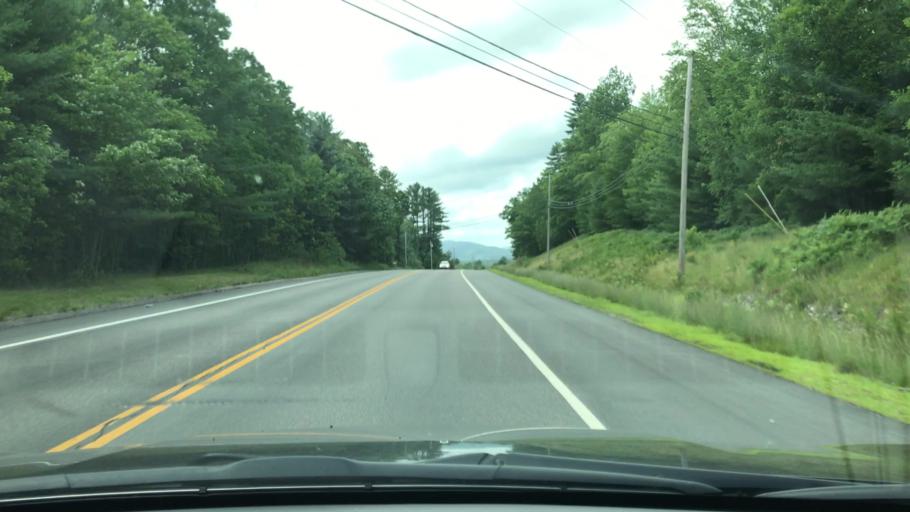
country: US
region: Maine
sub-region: Oxford County
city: Bethel
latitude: 44.4067
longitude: -70.7205
